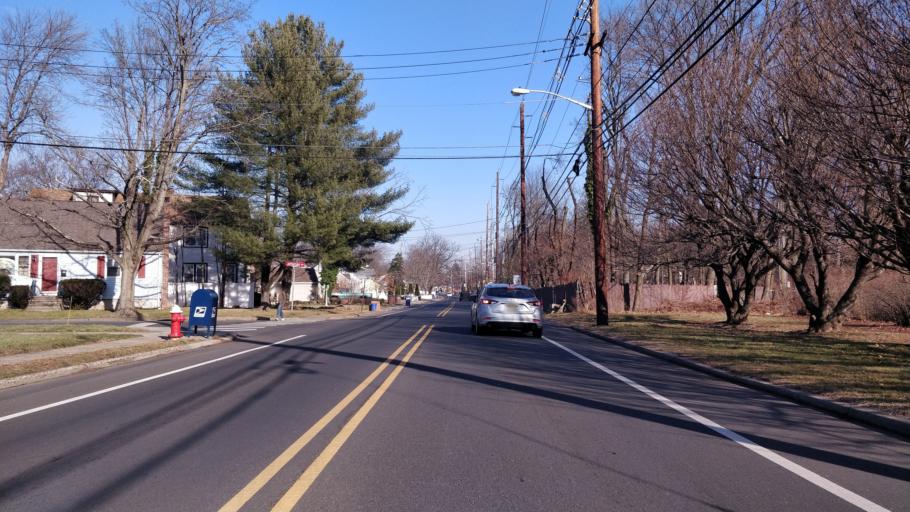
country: US
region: New Jersey
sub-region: Somerset County
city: North Plainfield
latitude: 40.6197
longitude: -74.4410
